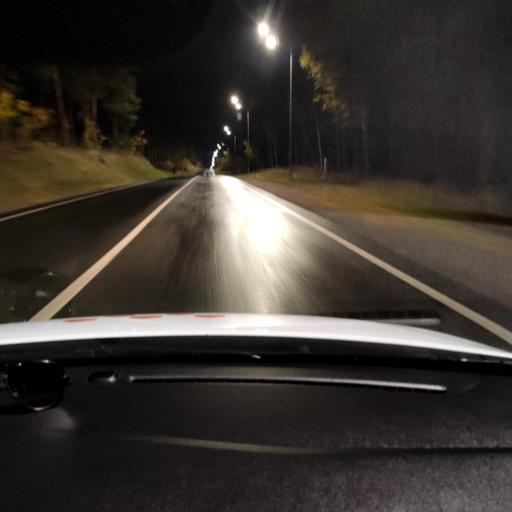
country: RU
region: Tatarstan
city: Verkhniy Uslon
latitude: 55.6375
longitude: 49.0515
